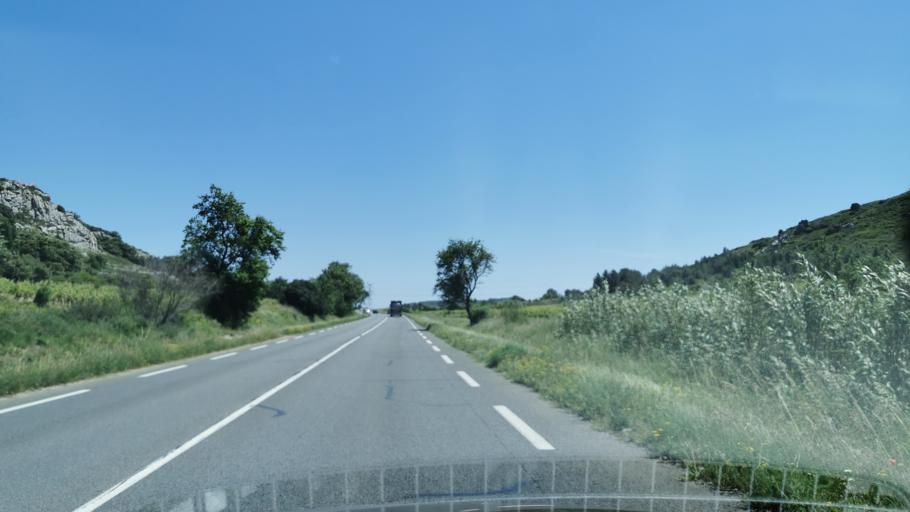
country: FR
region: Languedoc-Roussillon
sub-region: Departement de l'Aude
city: Nevian
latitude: 43.2045
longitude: 2.8882
